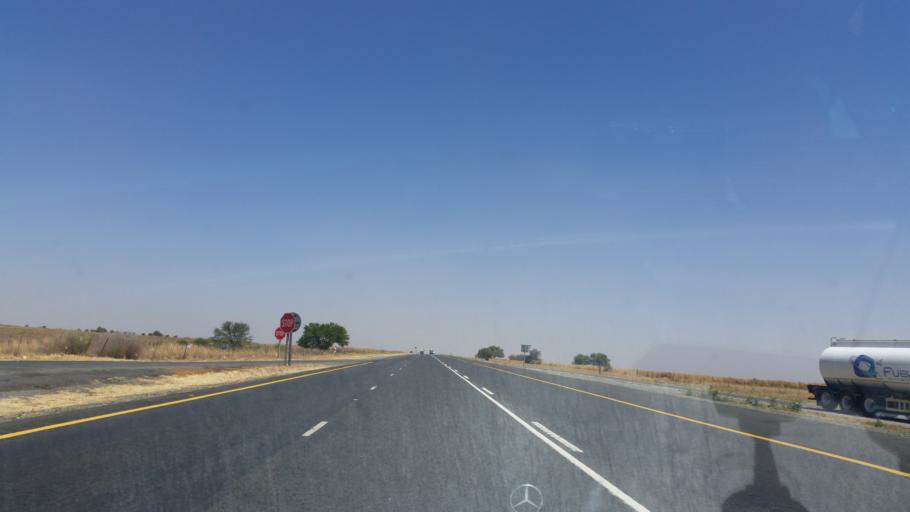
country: ZA
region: Orange Free State
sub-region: Lejweleputswa District Municipality
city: Winburg
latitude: -28.6425
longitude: 26.8876
